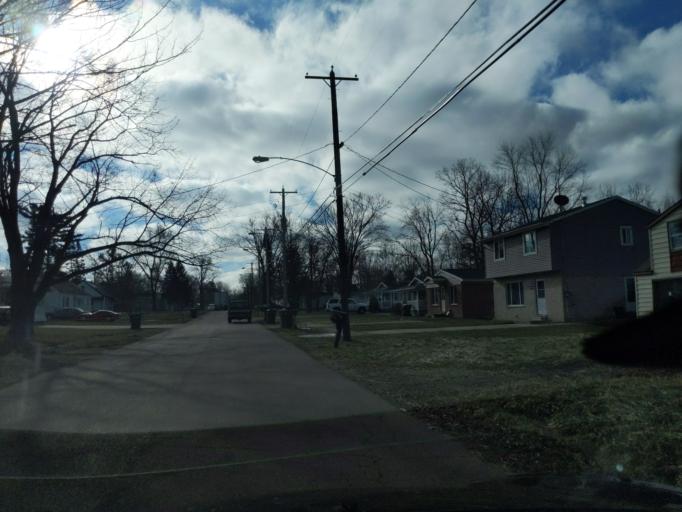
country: US
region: Michigan
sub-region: Ingham County
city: Lansing
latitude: 42.6870
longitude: -84.5771
